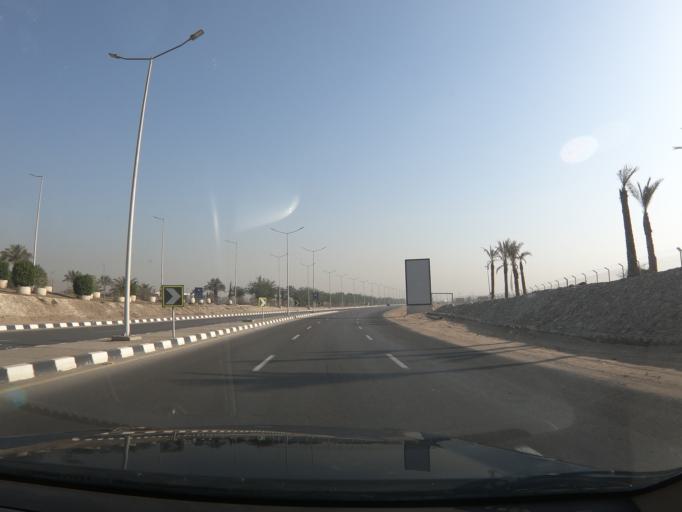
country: EG
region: Muhafazat al Qalyubiyah
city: Al Khankah
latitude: 30.0977
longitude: 31.3849
